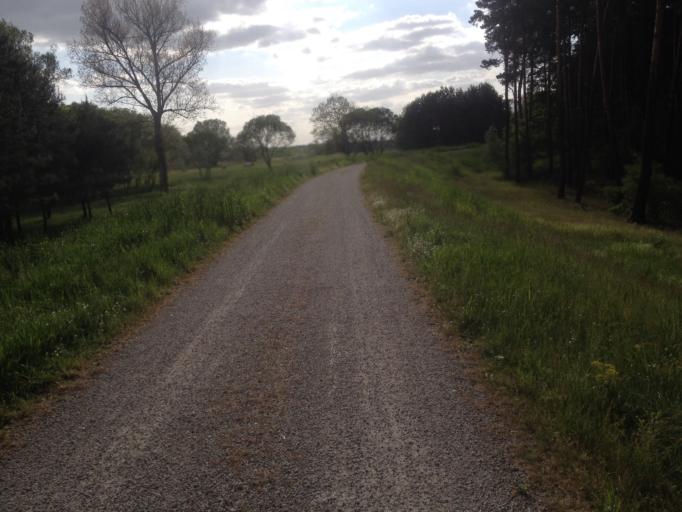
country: DE
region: Brandenburg
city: Drehnow
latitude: 51.8484
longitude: 14.3285
